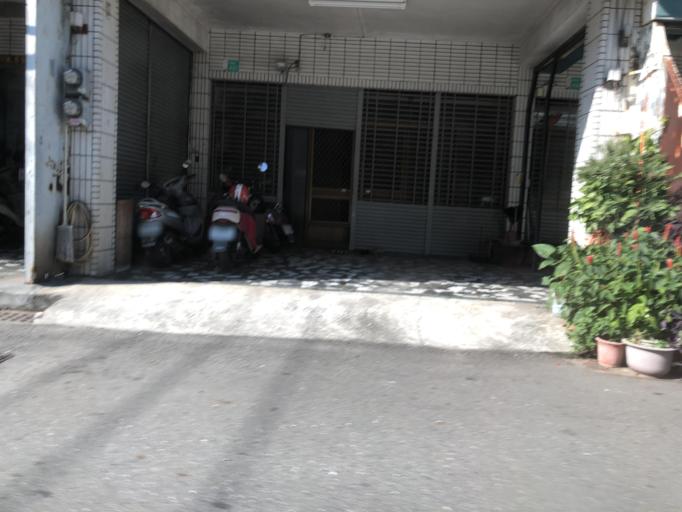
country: TW
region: Taiwan
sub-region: Tainan
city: Tainan
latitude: 23.0190
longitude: 120.2437
